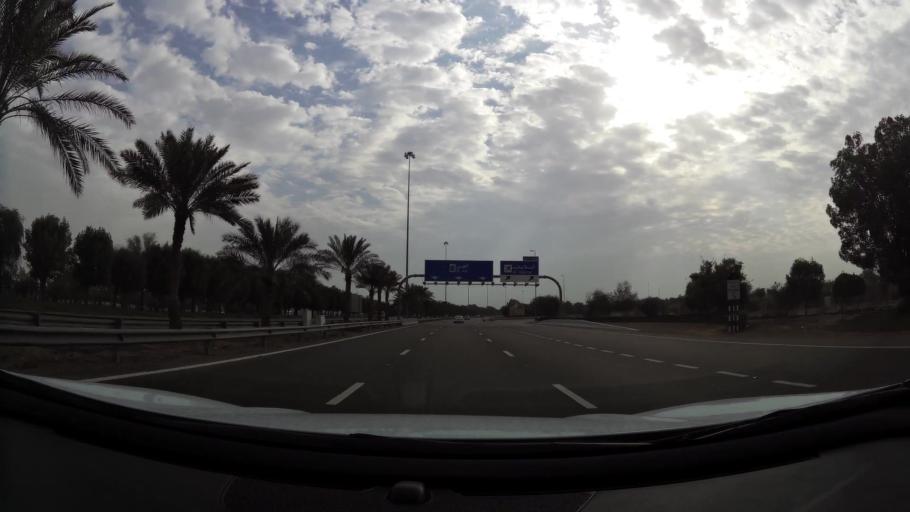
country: AE
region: Abu Dhabi
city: Al Ain
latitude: 24.2020
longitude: 55.5761
